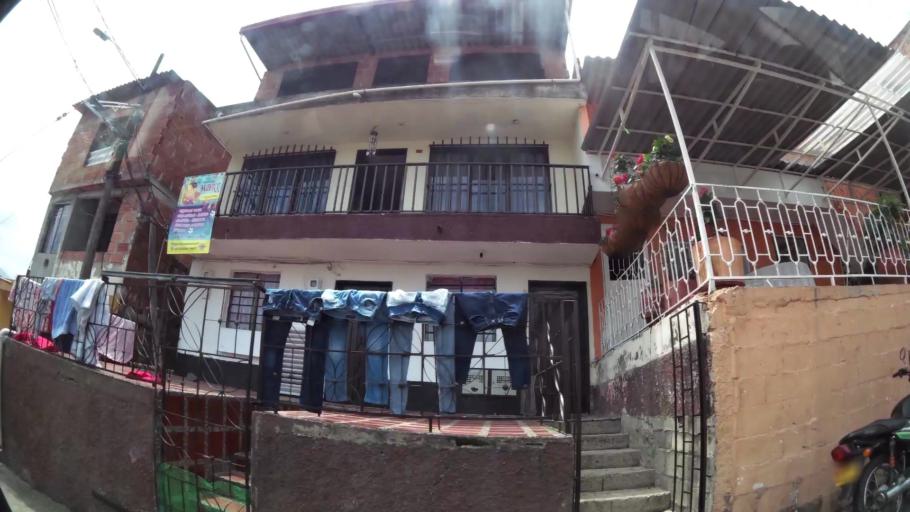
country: CO
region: Antioquia
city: Bello
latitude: 6.3119
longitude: -75.5781
